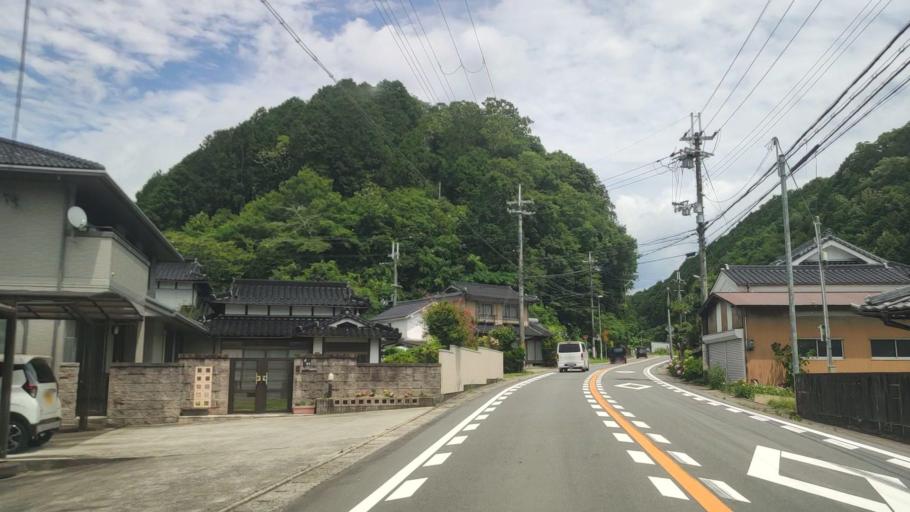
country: JP
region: Hyogo
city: Yamazakicho-nakabirose
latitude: 34.9930
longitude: 134.3988
